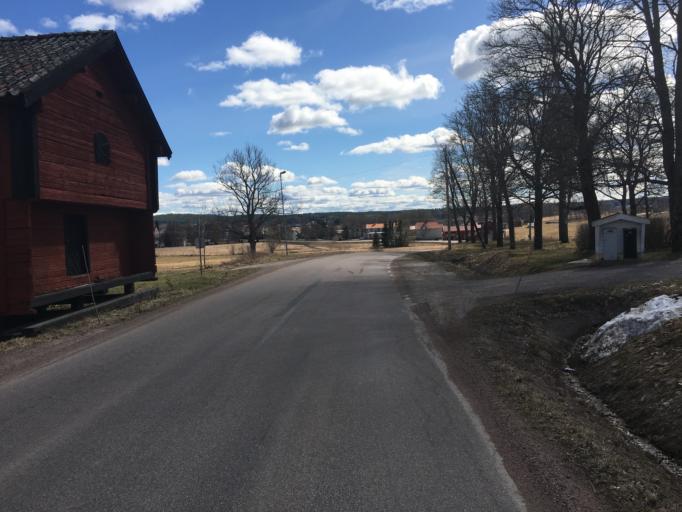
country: SE
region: Gaevleborg
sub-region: Hofors Kommun
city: Hofors
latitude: 60.5124
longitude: 16.4581
